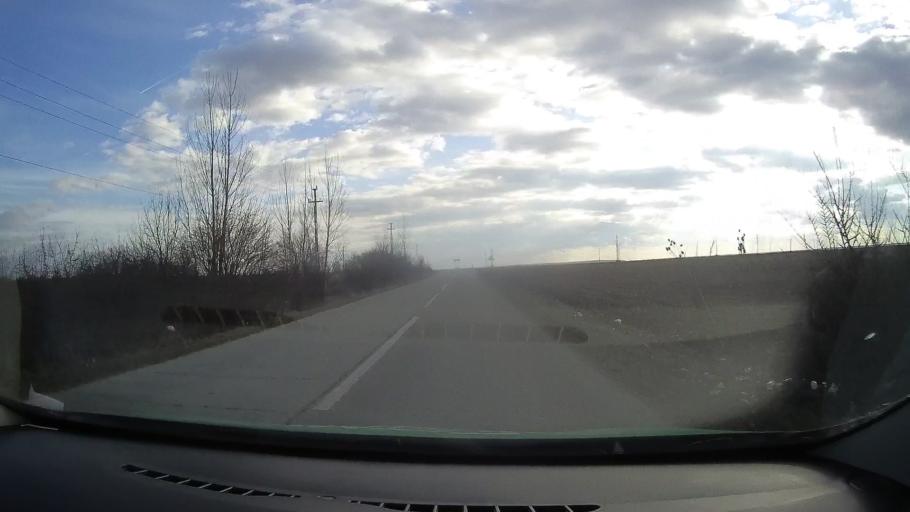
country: RO
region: Dambovita
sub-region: Comuna Ulmi
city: Viisoara
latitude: 44.8865
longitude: 25.4646
